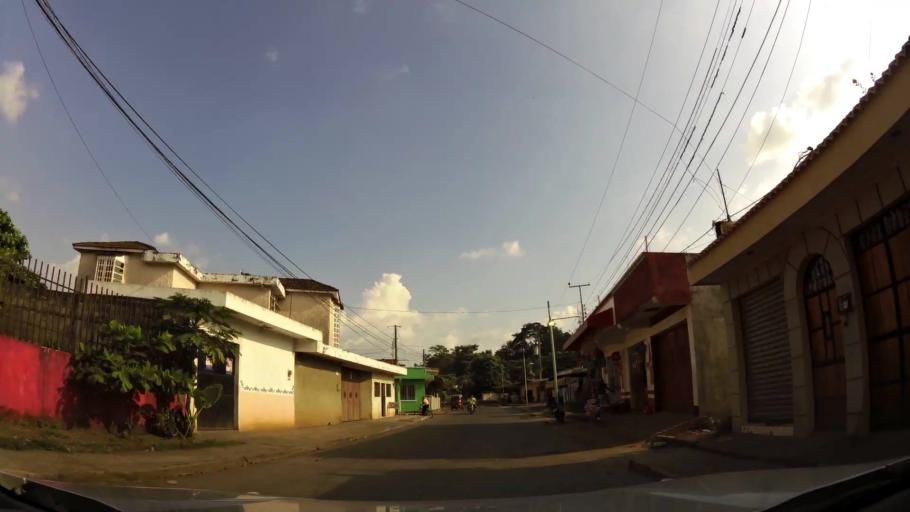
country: GT
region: Retalhuleu
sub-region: Municipio de Retalhuleu
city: Retalhuleu
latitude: 14.5299
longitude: -91.6755
